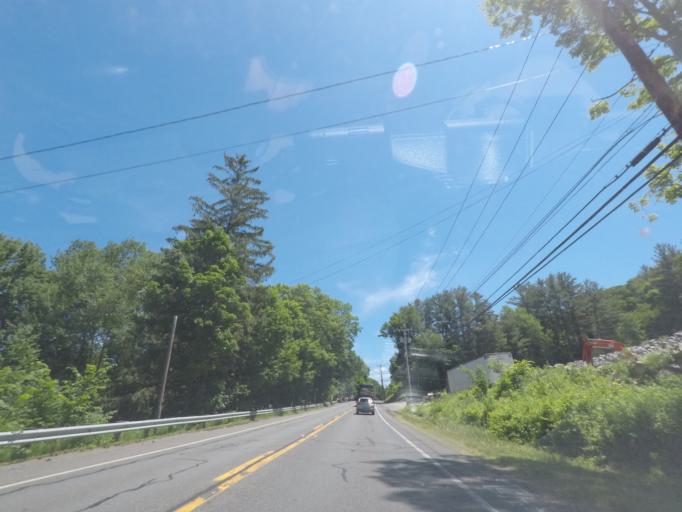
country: US
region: Massachusetts
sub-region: Berkshire County
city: Lee
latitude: 42.2989
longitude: -73.2026
